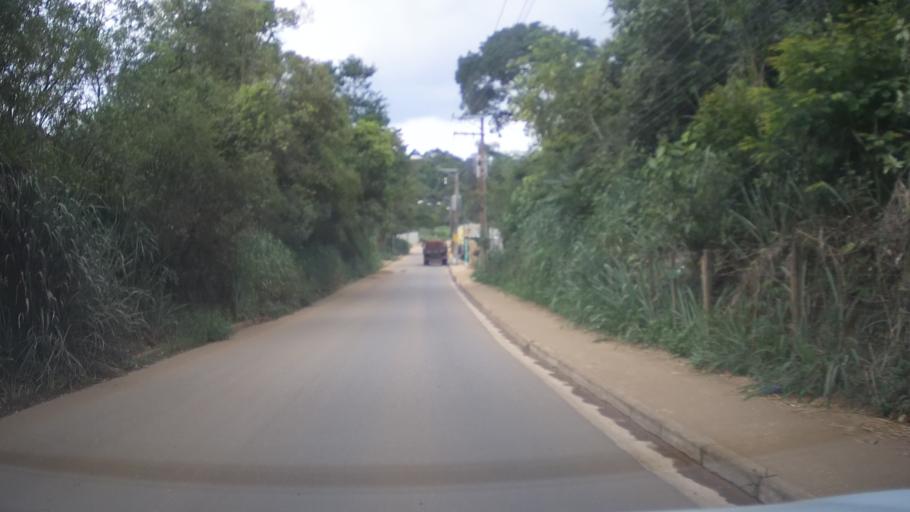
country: BR
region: Sao Paulo
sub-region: Aruja
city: Aruja
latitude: -23.3804
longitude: -46.3977
